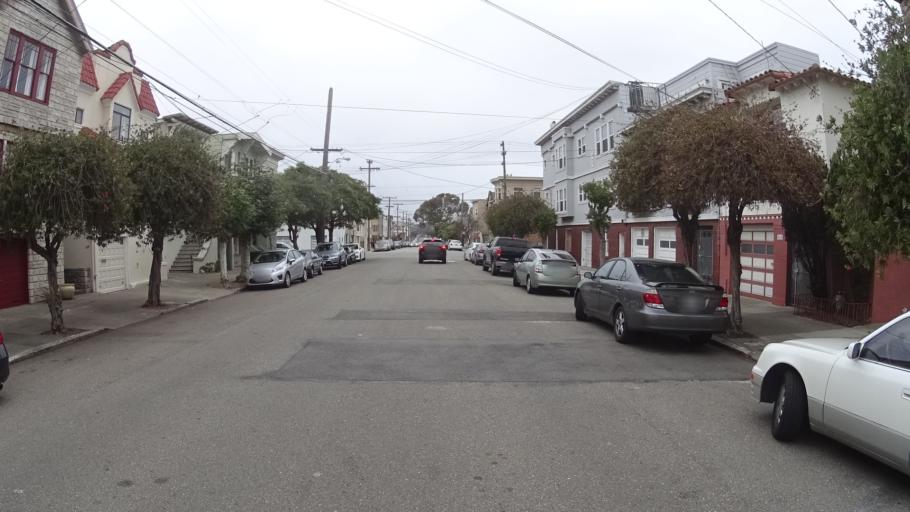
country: US
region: California
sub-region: San Francisco County
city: San Francisco
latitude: 37.7779
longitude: -122.4781
